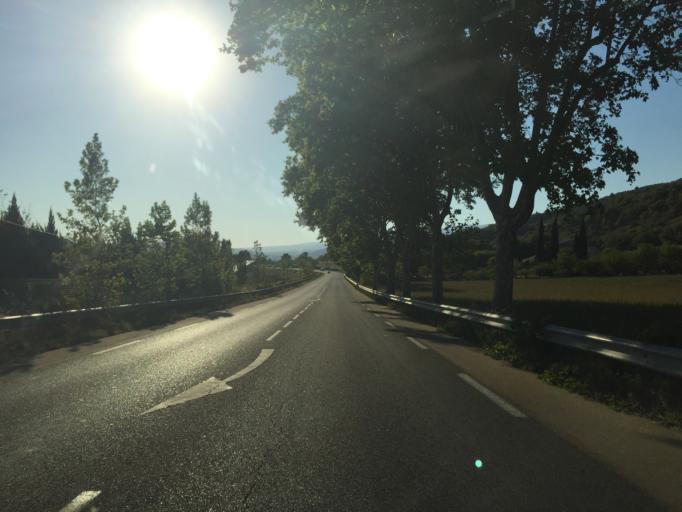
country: FR
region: Provence-Alpes-Cote d'Azur
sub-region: Departement des Alpes-de-Haute-Provence
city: Malijai
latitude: 44.0460
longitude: 6.0526
